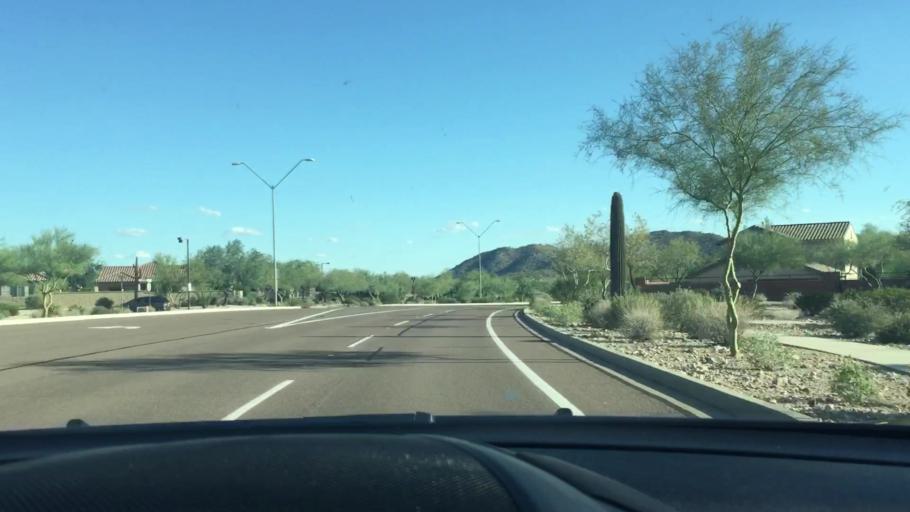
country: US
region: Arizona
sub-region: Maricopa County
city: Sun City West
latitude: 33.7357
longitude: -112.2546
